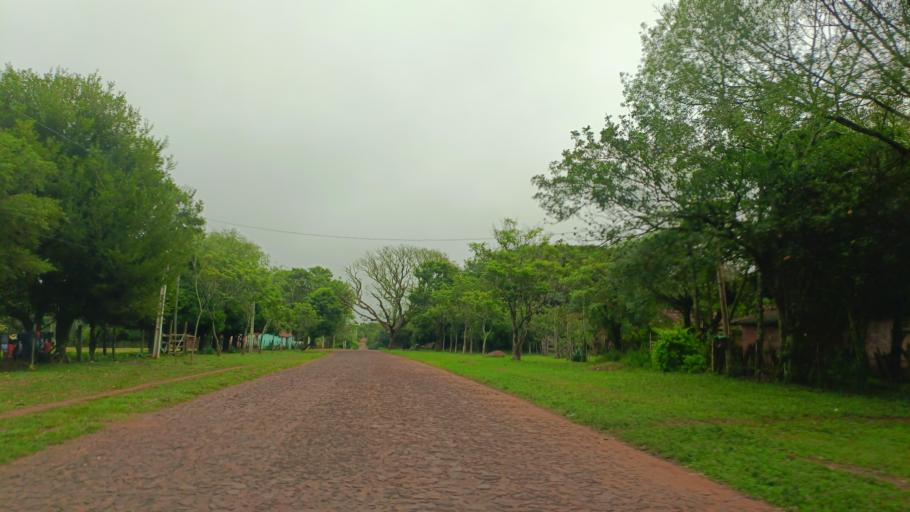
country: PY
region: Misiones
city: Santa Maria
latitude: -26.8615
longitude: -57.0267
